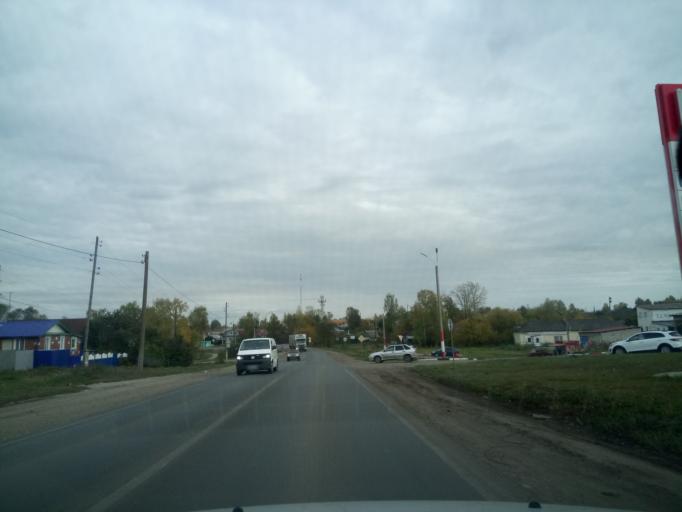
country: RU
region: Nizjnij Novgorod
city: Lukoyanov
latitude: 55.0298
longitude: 44.4662
